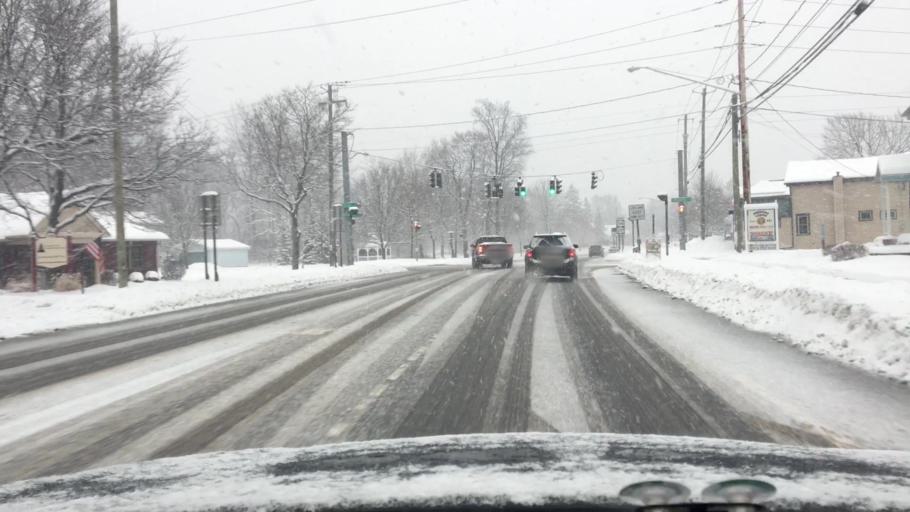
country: US
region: New York
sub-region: Erie County
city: Orchard Park
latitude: 42.7822
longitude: -78.7463
